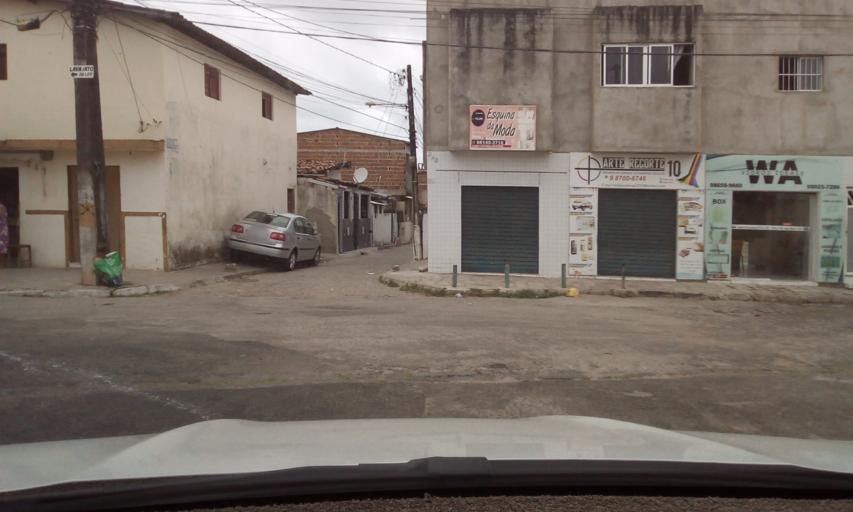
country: BR
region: Paraiba
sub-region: Joao Pessoa
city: Joao Pessoa
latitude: -7.1003
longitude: -34.8545
